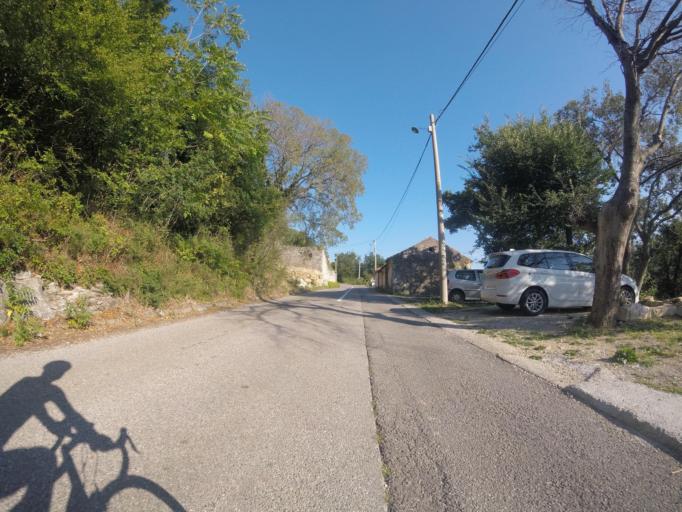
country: HR
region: Primorsko-Goranska
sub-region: Grad Crikvenica
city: Crikvenica
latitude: 45.2235
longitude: 14.6853
